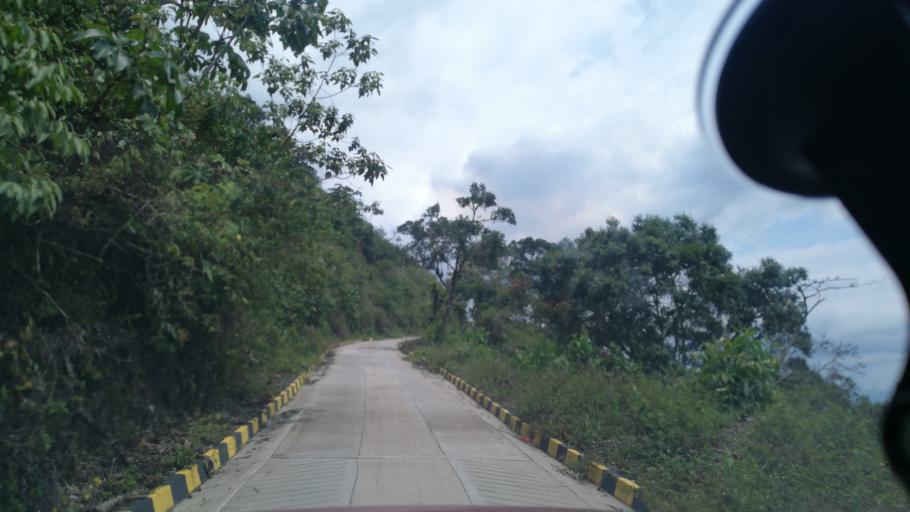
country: CO
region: Cundinamarca
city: Vergara
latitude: 5.1999
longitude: -74.2765
